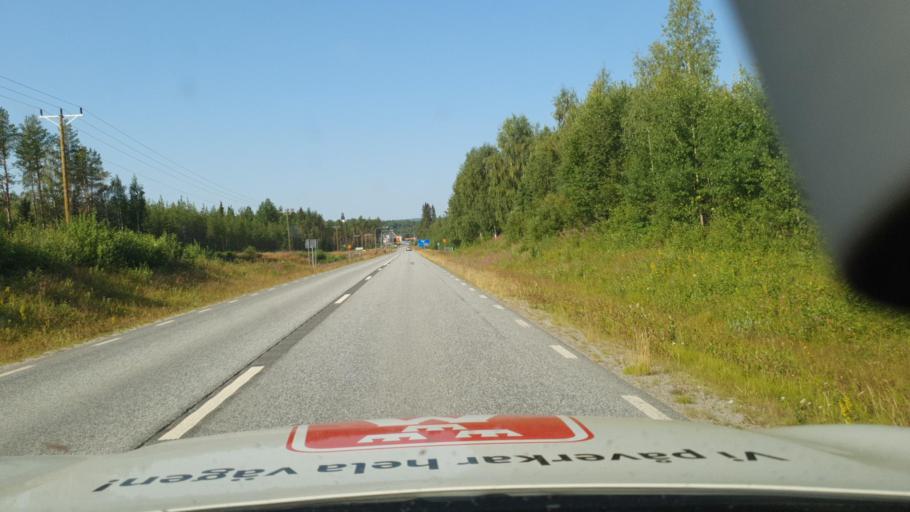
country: SE
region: Vaesterbotten
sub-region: Asele Kommun
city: Asele
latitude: 64.1717
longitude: 17.3849
